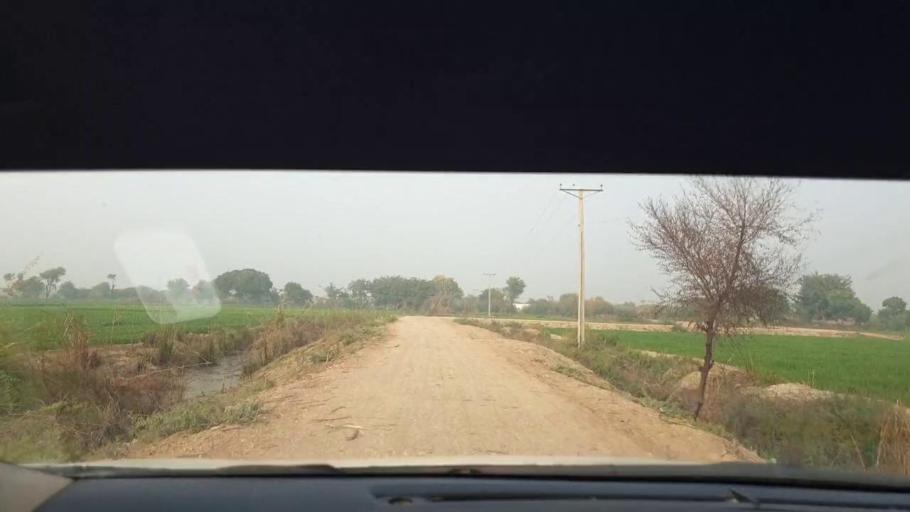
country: PK
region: Sindh
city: Berani
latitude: 25.8002
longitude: 68.8518
